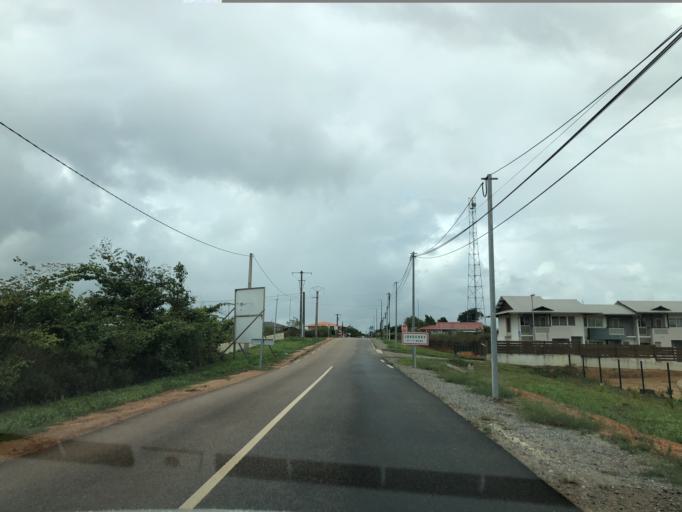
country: GF
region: Guyane
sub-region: Guyane
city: Mana
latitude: 5.6026
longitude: -53.8178
